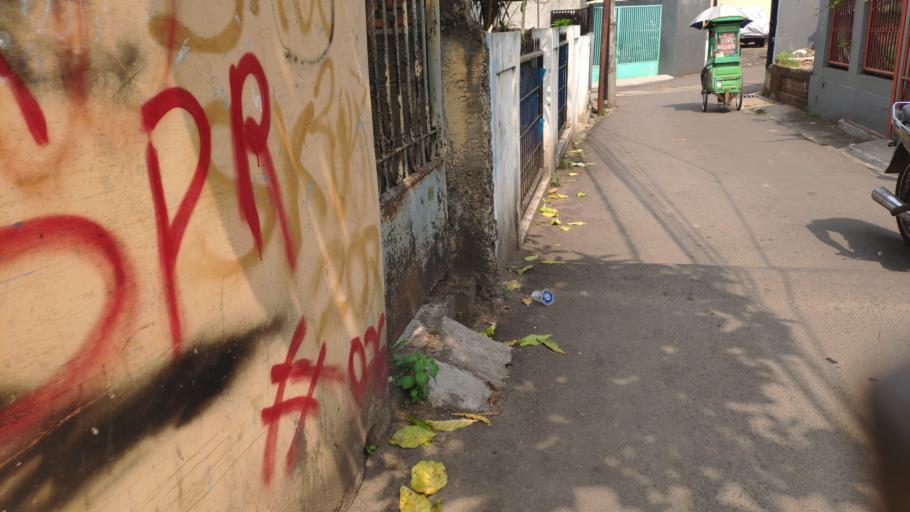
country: ID
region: West Java
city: Depok
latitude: -6.3187
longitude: 106.8269
